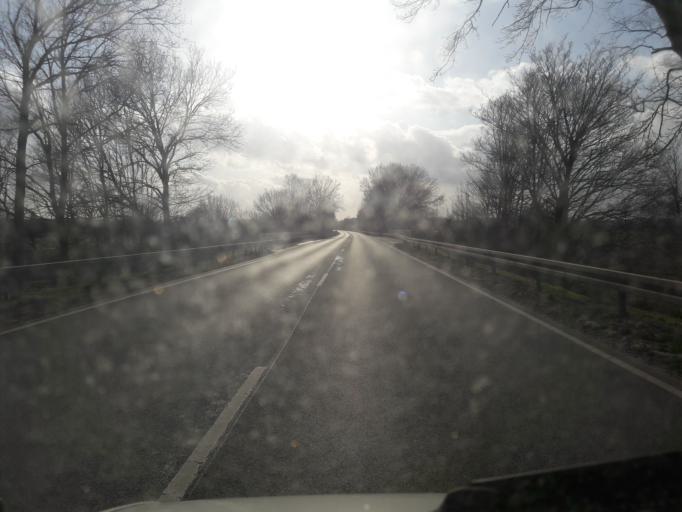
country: DE
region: Lower Saxony
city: Uchte
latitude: 52.5014
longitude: 8.8974
